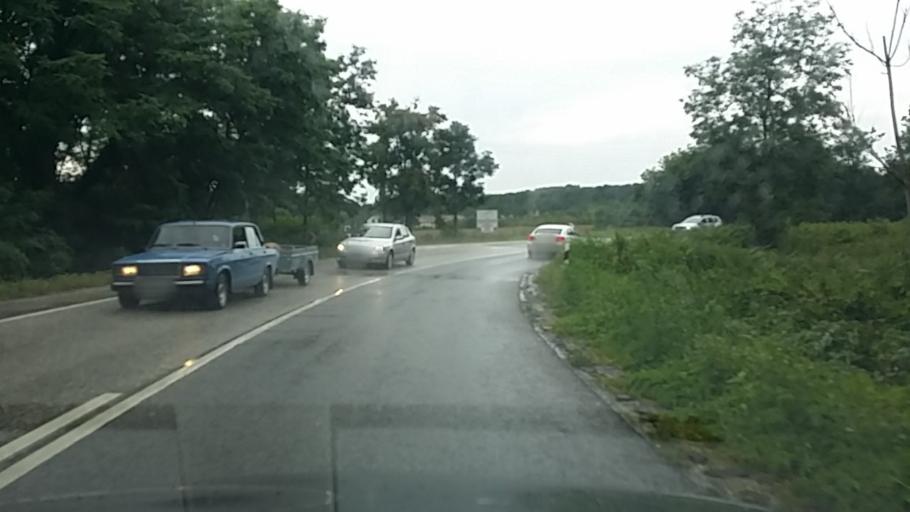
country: HU
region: Pest
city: Ullo
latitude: 47.3495
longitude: 19.3077
